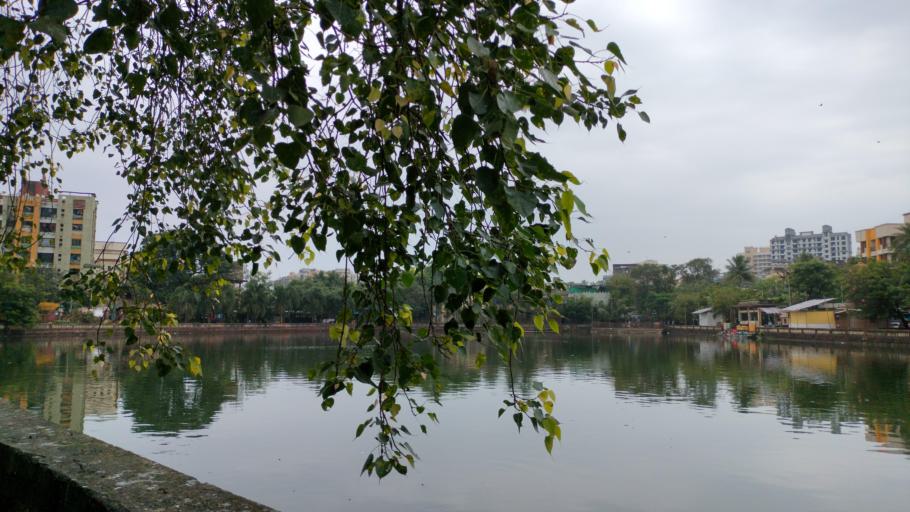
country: IN
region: Maharashtra
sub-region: Thane
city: Virar
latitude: 19.4147
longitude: 72.8610
